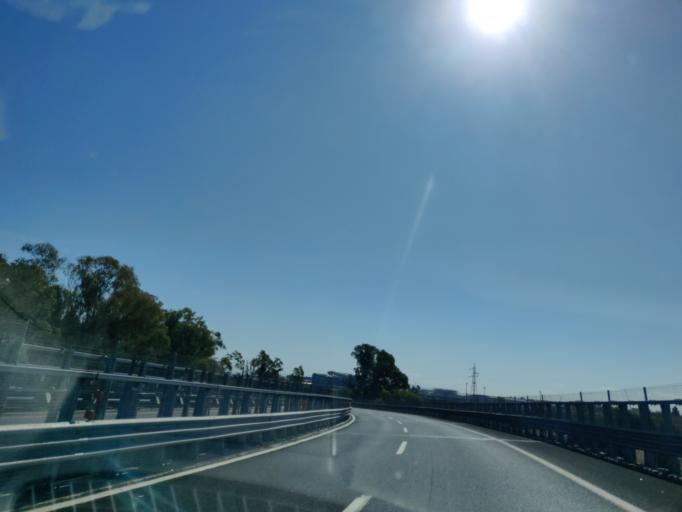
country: IT
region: Latium
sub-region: Citta metropolitana di Roma Capitale
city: Npp 23 (Parco Leonardo)
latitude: 41.8096
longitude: 12.3102
